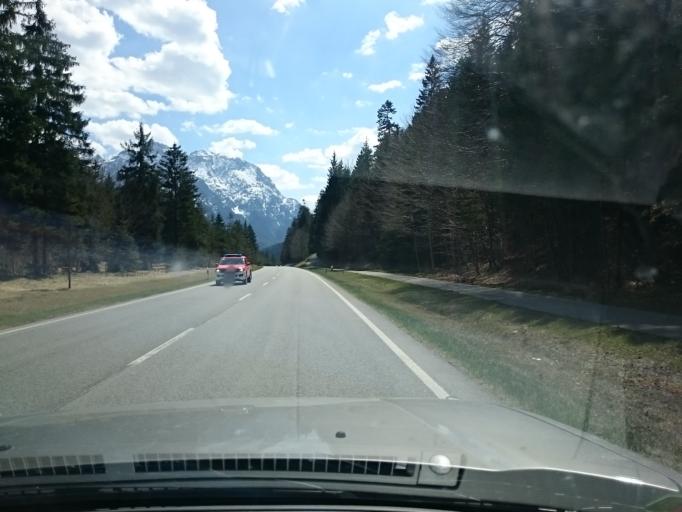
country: DE
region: Bavaria
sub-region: Upper Bavaria
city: Krun
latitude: 47.4890
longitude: 11.2745
